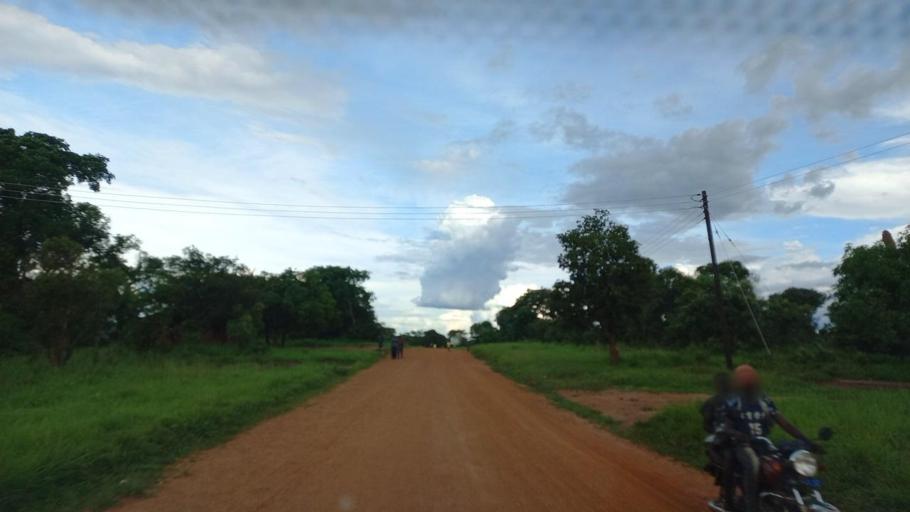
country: ZM
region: North-Western
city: Mwinilunga
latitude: -11.7587
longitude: 24.4259
